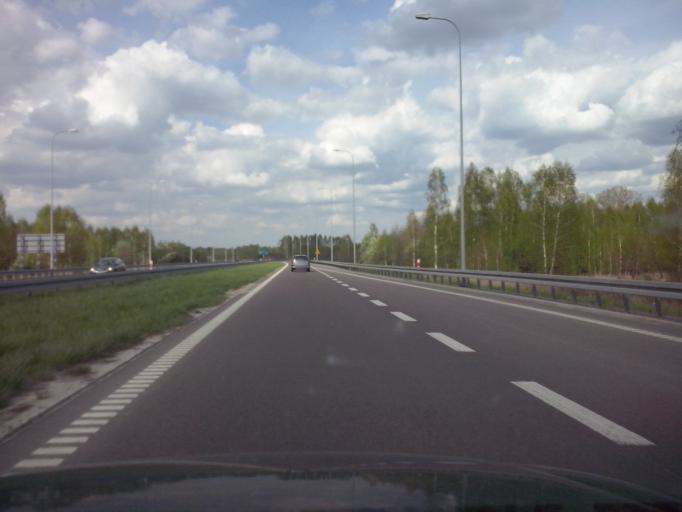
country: PL
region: Subcarpathian Voivodeship
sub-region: Powiat rzeszowski
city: Wolka Podlesna
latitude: 50.1192
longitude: 22.0781
